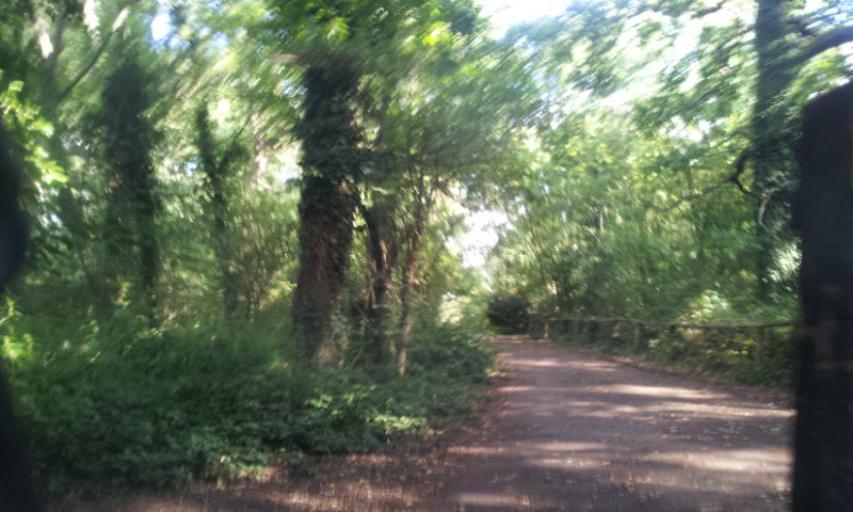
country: GB
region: England
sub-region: Greater London
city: Chislehurst
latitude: 51.3938
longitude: 0.0636
